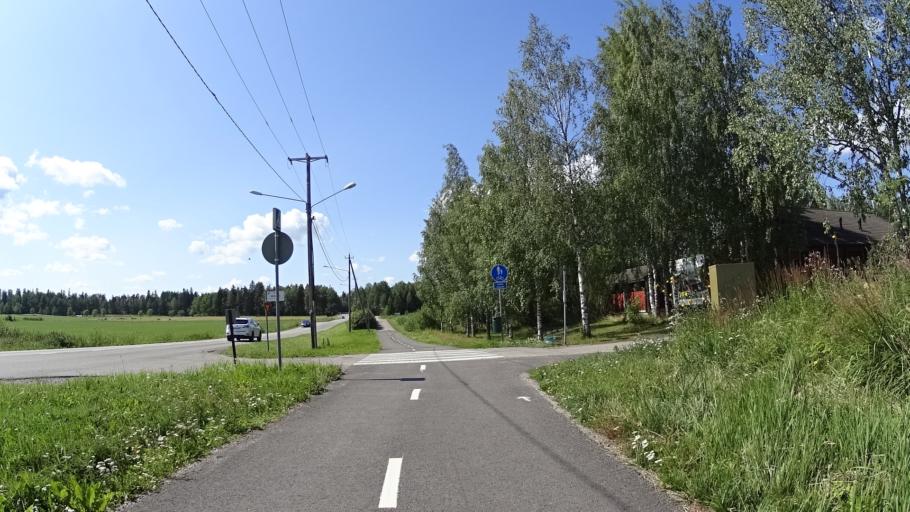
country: FI
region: Uusimaa
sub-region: Helsinki
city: Jaervenpaeae
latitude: 60.4638
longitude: 25.0633
